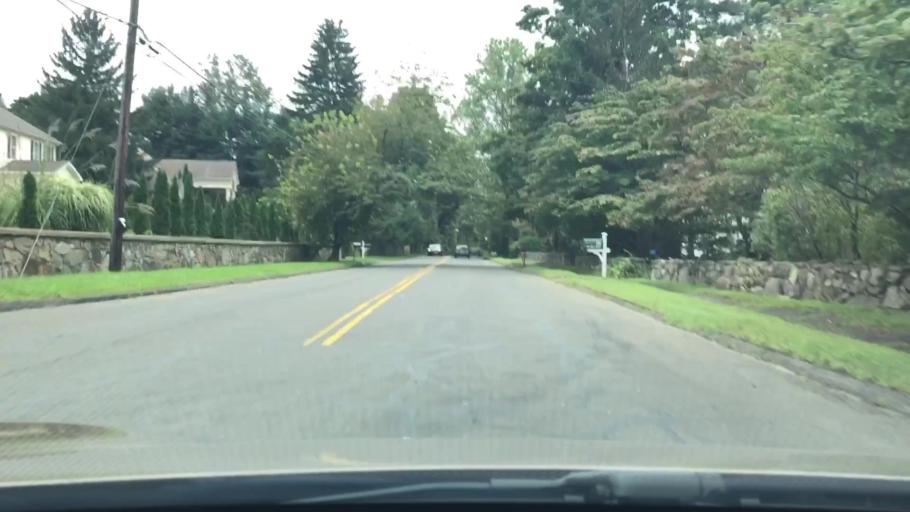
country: US
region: Connecticut
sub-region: Fairfield County
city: Norwalk
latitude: 41.1262
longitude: -73.4524
